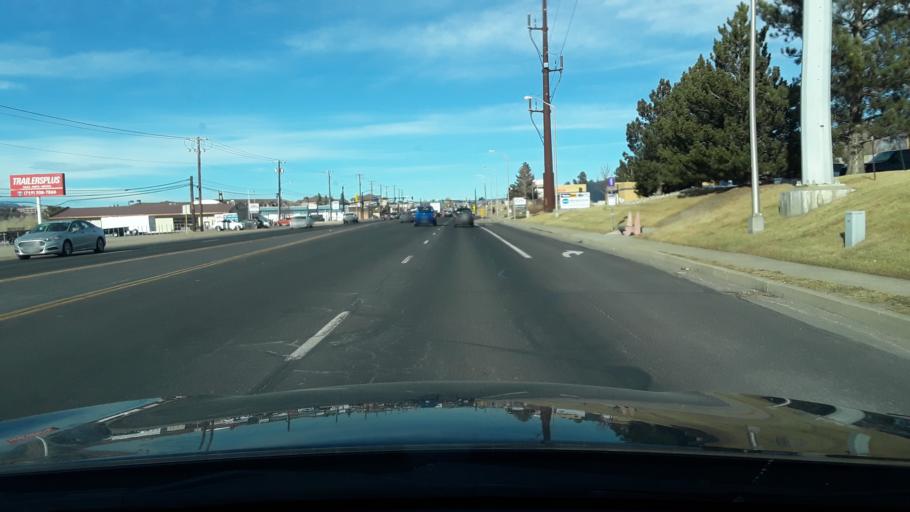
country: US
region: Colorado
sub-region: El Paso County
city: Colorado Springs
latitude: 38.8952
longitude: -104.8184
